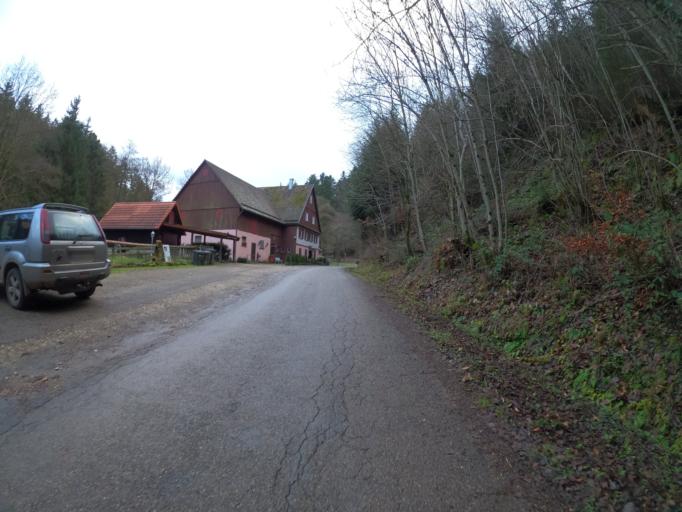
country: DE
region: Baden-Wuerttemberg
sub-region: Regierungsbezirk Stuttgart
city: Waschenbeuren
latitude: 48.7722
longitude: 9.7129
